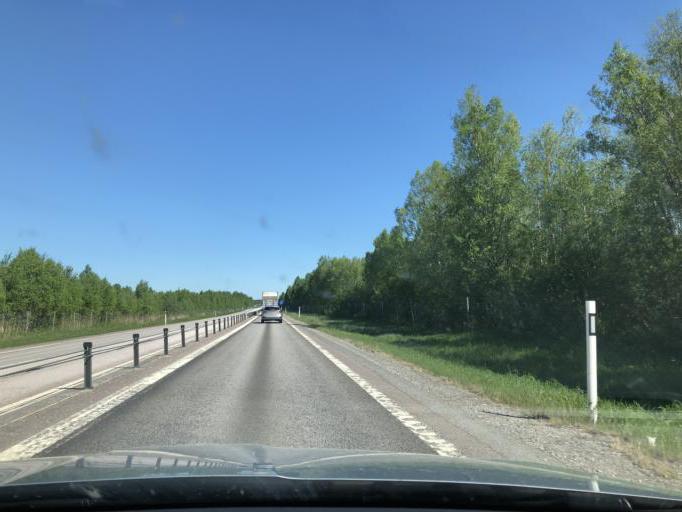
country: SE
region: Norrbotten
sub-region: Lulea Kommun
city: Lulea
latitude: 65.7289
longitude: 22.1537
